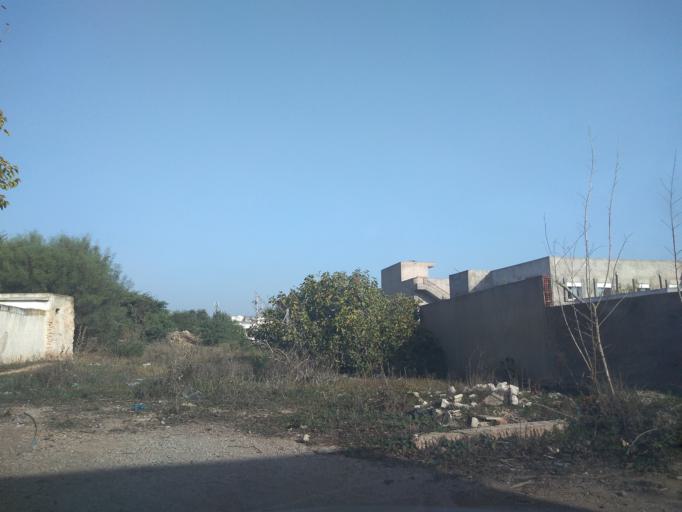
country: TN
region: Manouba
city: Manouba
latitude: 36.7927
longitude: 10.0853
